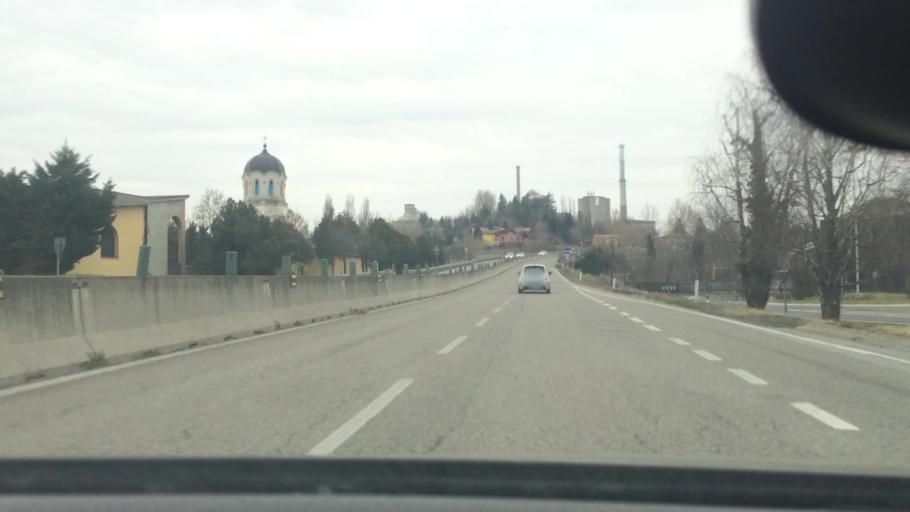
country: IT
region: Lombardy
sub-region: Provincia di Como
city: Merone
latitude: 45.7884
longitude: 9.2427
